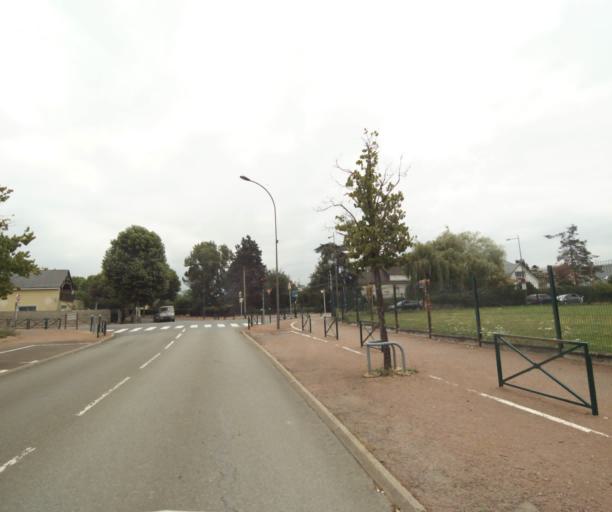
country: FR
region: Pays de la Loire
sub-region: Departement de la Sarthe
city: Sable-sur-Sarthe
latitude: 47.8321
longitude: -0.3201
